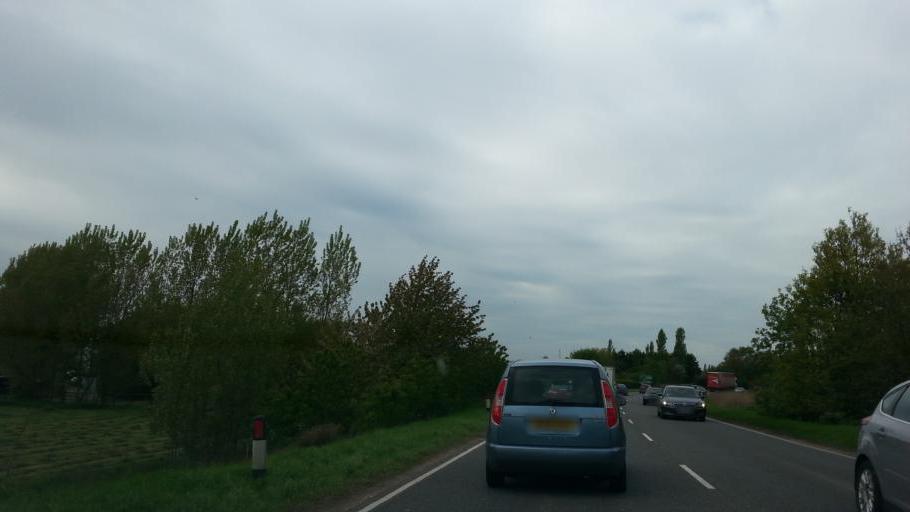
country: GB
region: England
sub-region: Cambridgeshire
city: March
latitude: 52.5555
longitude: 0.0669
